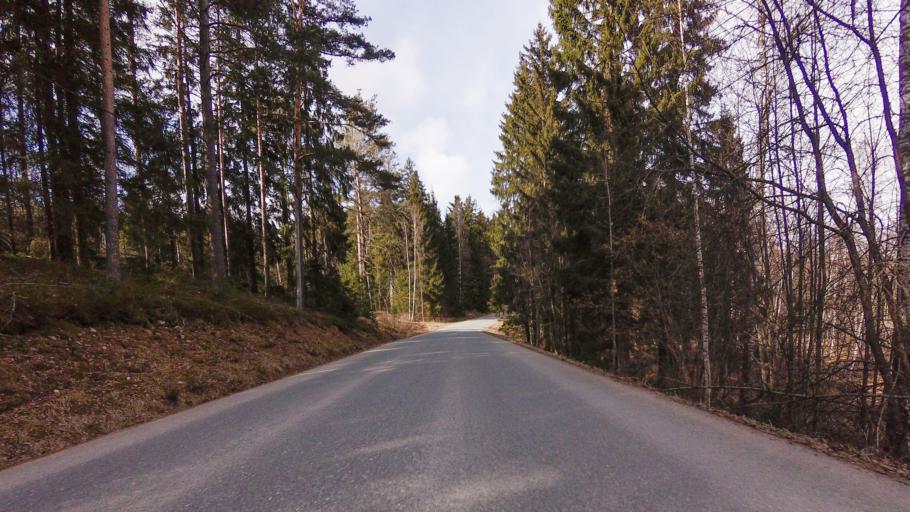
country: FI
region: Varsinais-Suomi
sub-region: Salo
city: Suomusjaervi
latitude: 60.3307
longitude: 23.7039
